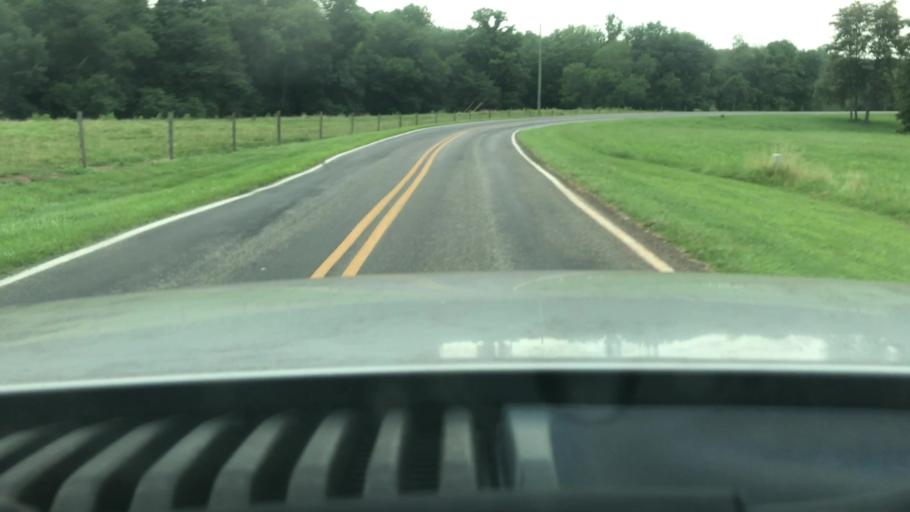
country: US
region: North Carolina
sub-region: Surry County
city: Dobson
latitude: 36.4177
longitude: -80.8227
